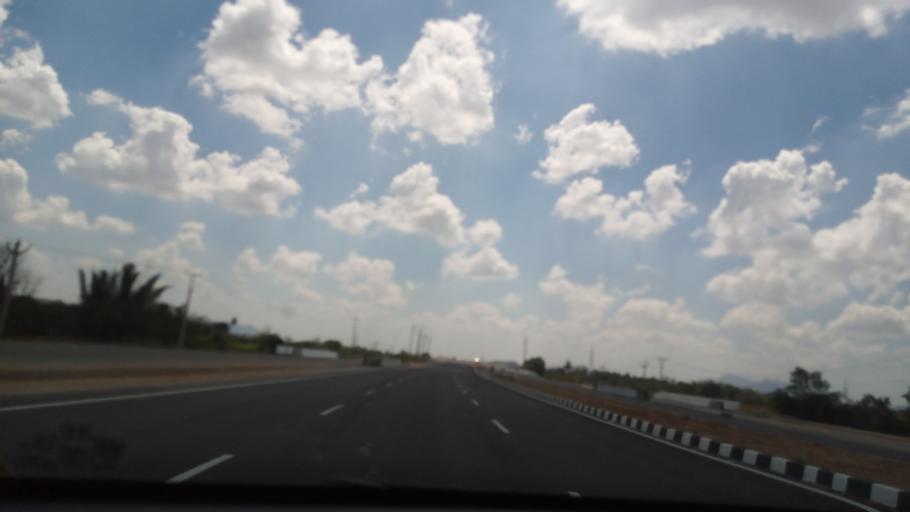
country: IN
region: Andhra Pradesh
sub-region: Chittoor
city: Pakala
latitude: 13.4241
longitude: 79.1248
